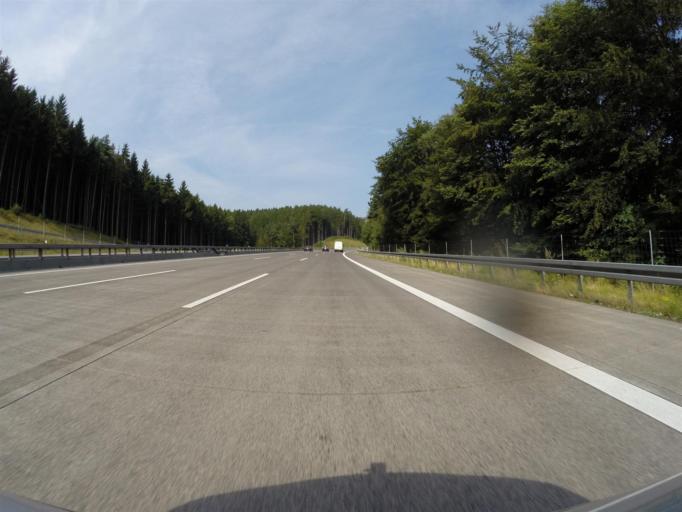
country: DE
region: Hesse
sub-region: Regierungsbezirk Kassel
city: Niederaula
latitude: 50.8474
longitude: 9.6319
